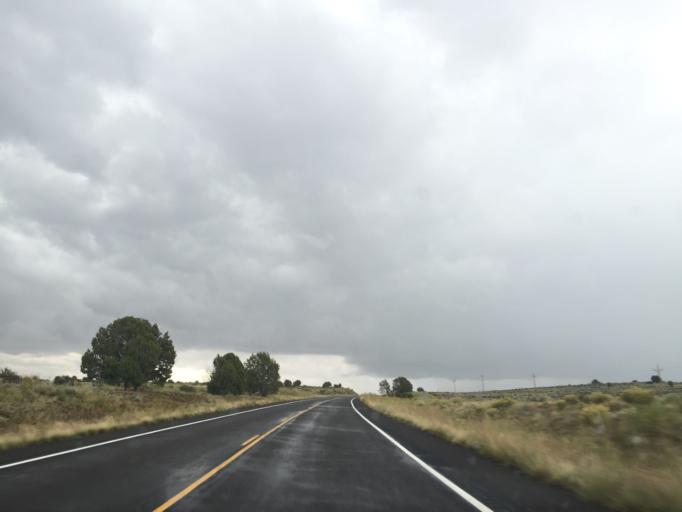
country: US
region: Utah
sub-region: Kane County
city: Kanab
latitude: 37.2306
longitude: -112.7313
